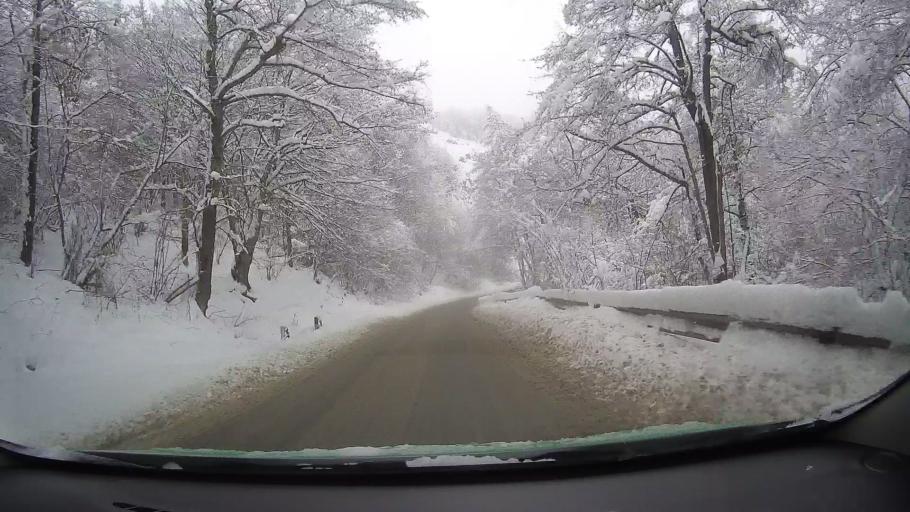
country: RO
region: Sibiu
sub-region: Comuna Tilisca
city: Tilisca
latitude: 45.8016
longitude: 23.8098
